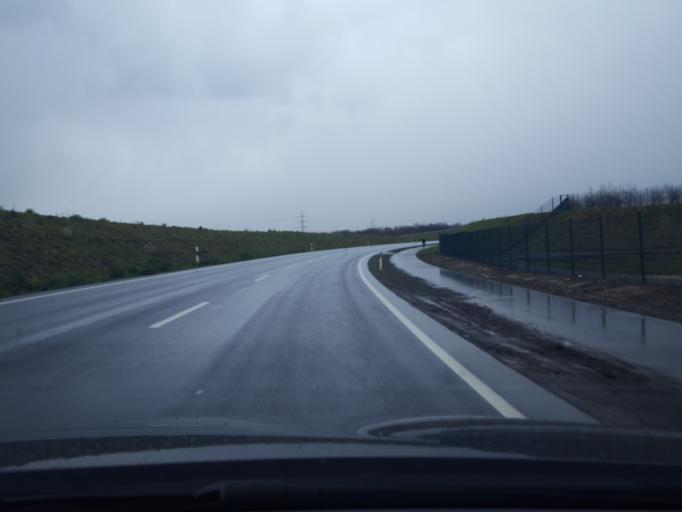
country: DE
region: North Rhine-Westphalia
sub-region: Regierungsbezirk Koln
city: Troisdorf
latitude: 50.7953
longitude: 7.1023
